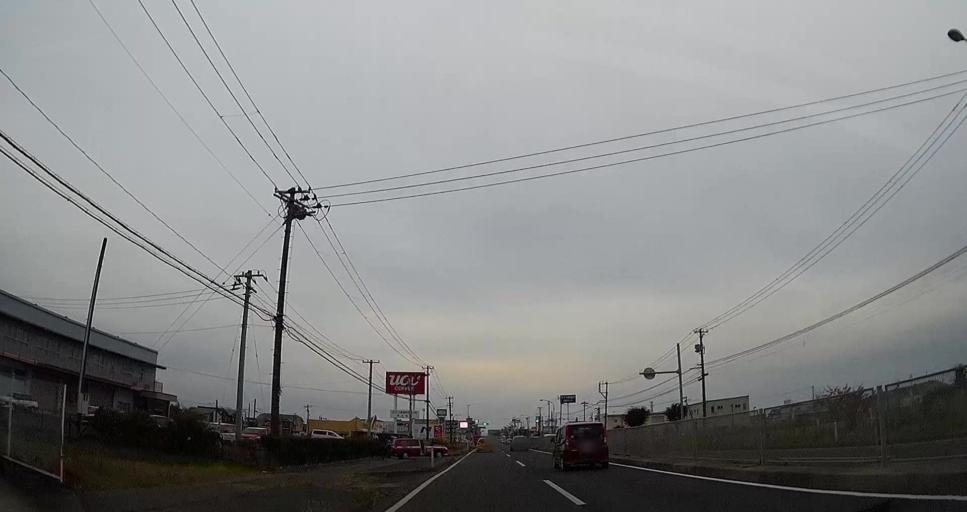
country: JP
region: Miyagi
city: Iwanuma
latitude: 38.1528
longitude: 140.8857
